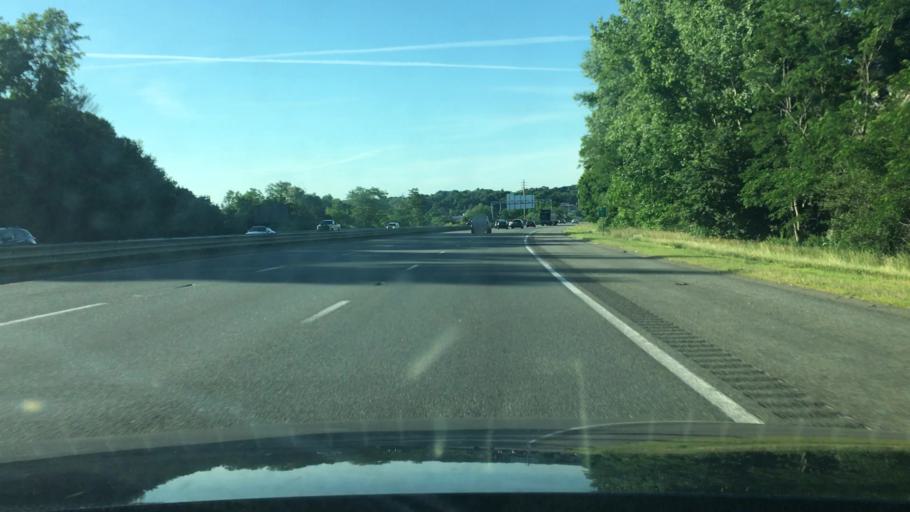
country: US
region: Massachusetts
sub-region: Essex County
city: South Peabody
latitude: 42.5385
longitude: -70.9843
